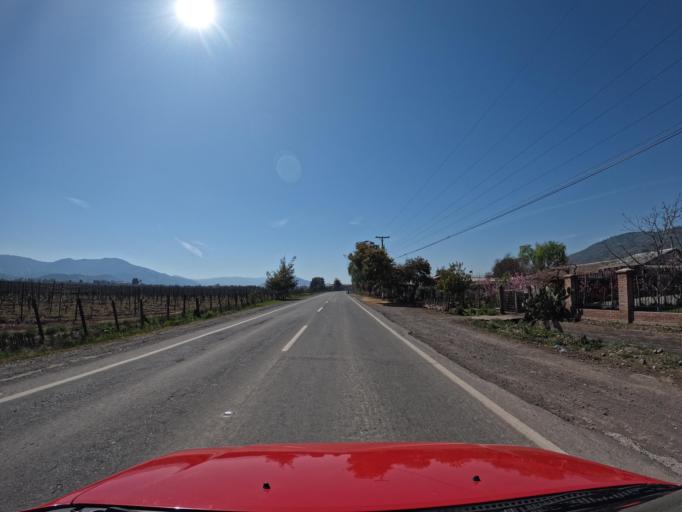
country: CL
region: Maule
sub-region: Provincia de Curico
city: Rauco
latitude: -35.0187
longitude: -71.4266
